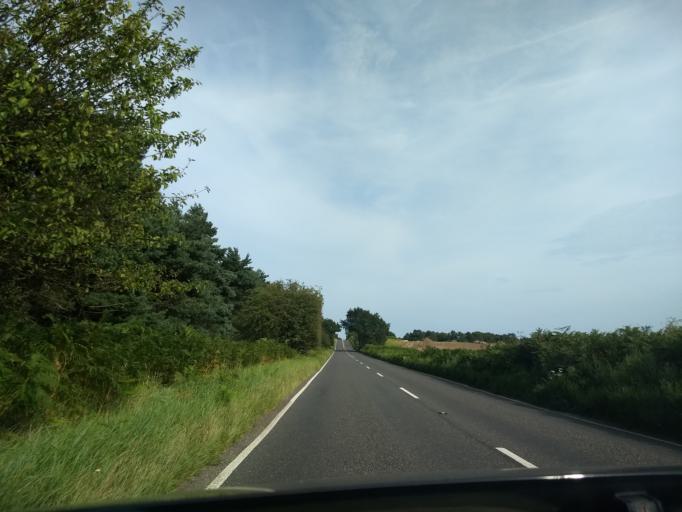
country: GB
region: England
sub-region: Suffolk
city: Woodbridge
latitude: 52.0873
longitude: 1.3663
